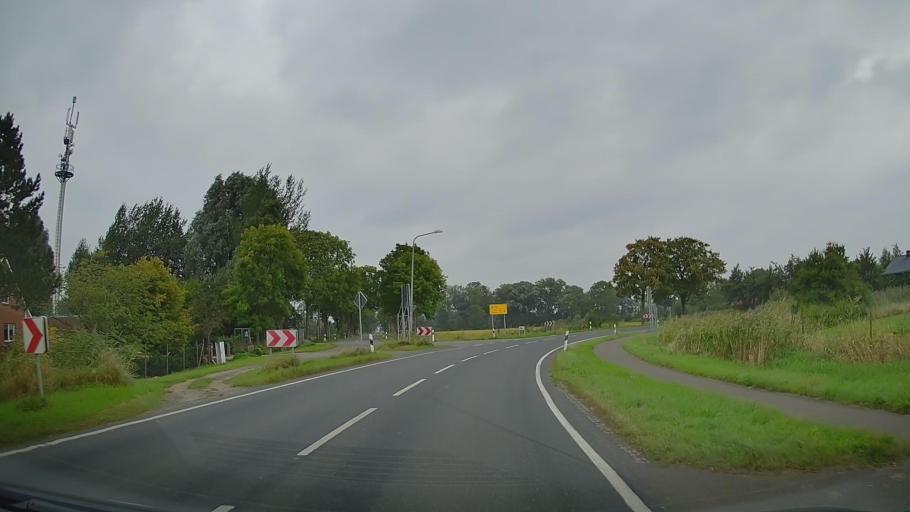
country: DE
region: Lower Saxony
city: Balje
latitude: 53.8217
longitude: 9.1320
